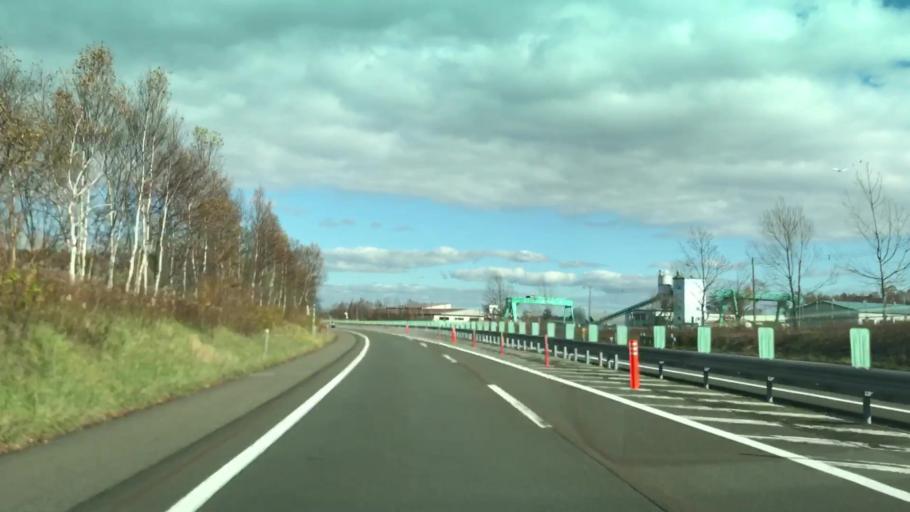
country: JP
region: Hokkaido
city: Chitose
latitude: 42.8542
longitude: 141.6001
